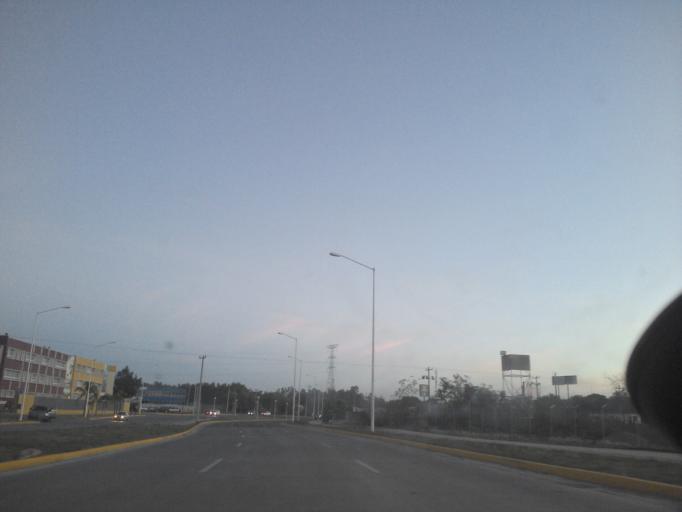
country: MX
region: Jalisco
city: Nuevo Mexico
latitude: 20.6962
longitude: -103.4616
